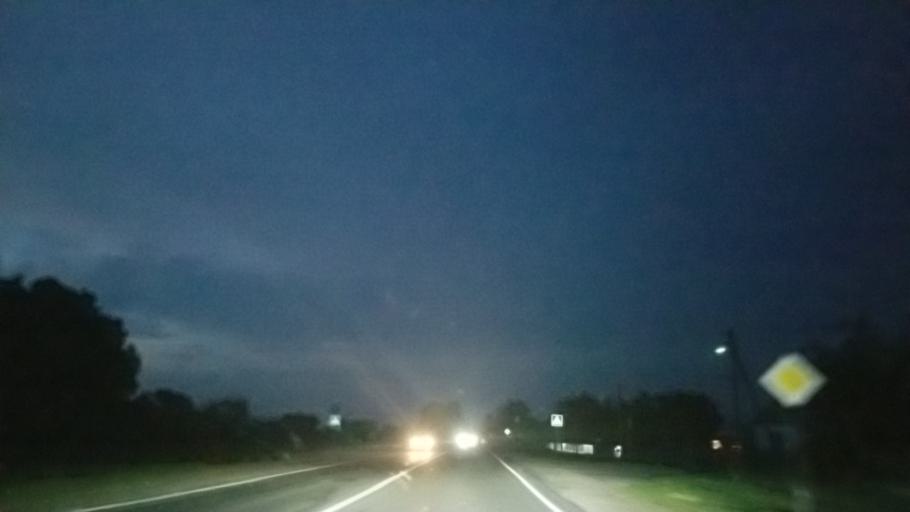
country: PL
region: Lublin Voivodeship
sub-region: Powiat bialski
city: Koden
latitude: 51.9403
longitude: 23.6645
